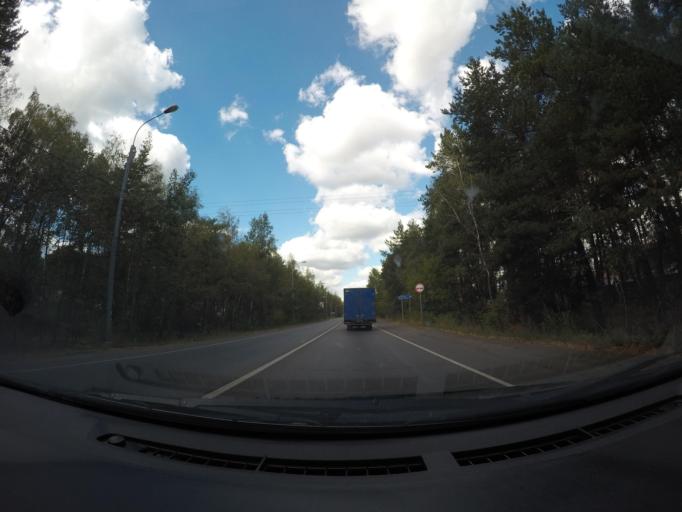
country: RU
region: Moskovskaya
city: Il'inskiy
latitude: 55.6488
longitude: 38.1320
